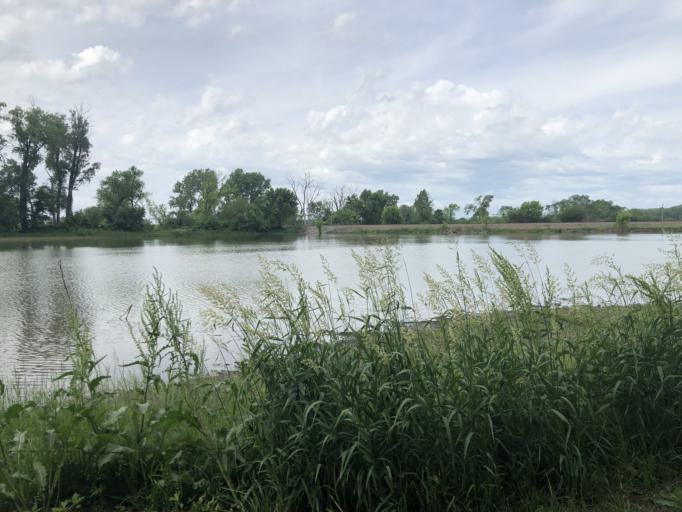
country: US
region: Missouri
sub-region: Platte County
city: Weston
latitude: 39.3725
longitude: -94.8722
